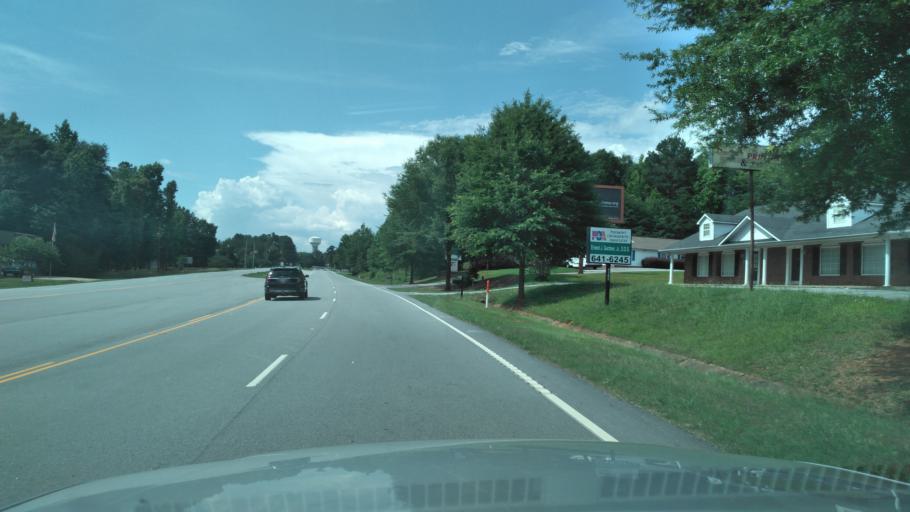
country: US
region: South Carolina
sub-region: Spartanburg County
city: Roebuck
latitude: 34.8814
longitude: -81.9564
